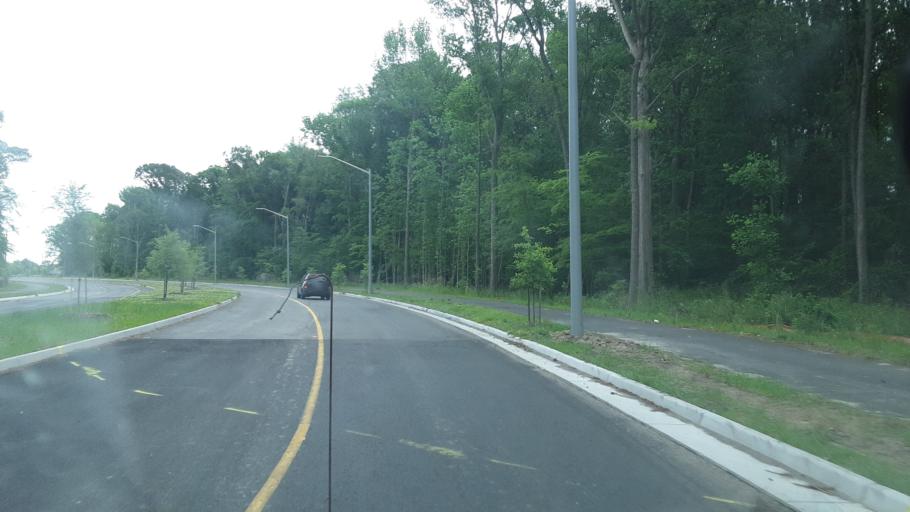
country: US
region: Virginia
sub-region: City of Virginia Beach
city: Virginia Beach
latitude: 36.7597
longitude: -76.0183
